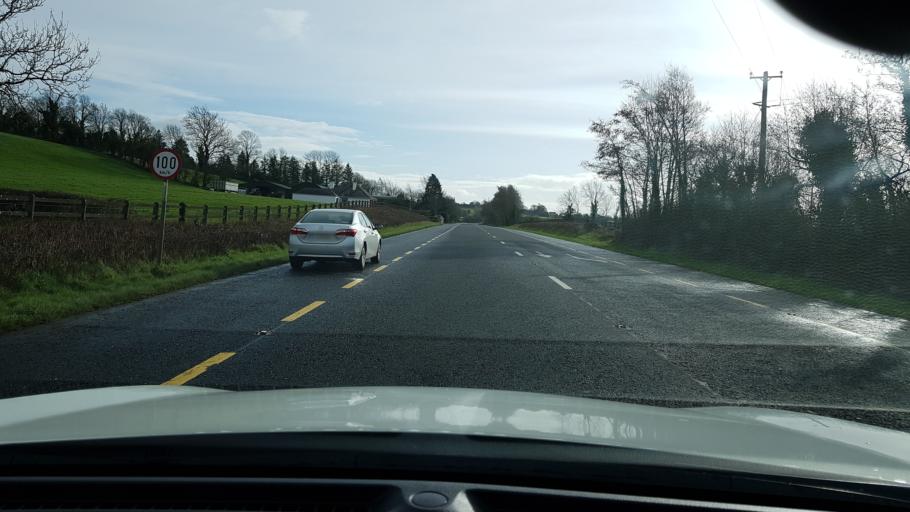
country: IE
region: Connaught
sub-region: County Leitrim
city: Carrick-on-Shannon
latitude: 53.9118
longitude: -7.9672
